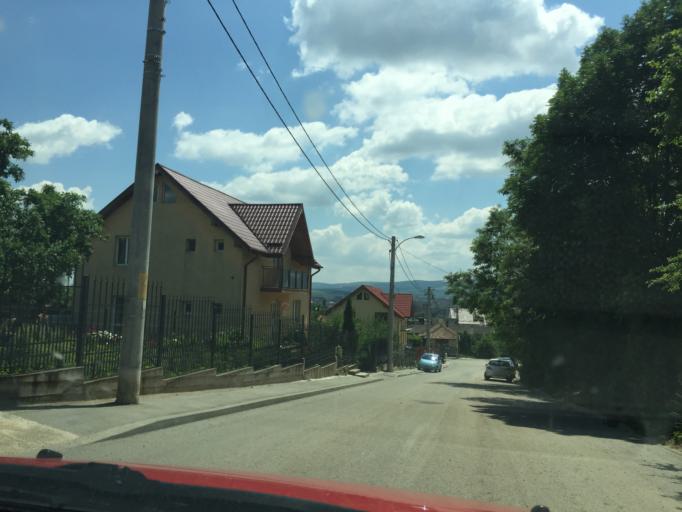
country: RO
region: Cluj
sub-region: Municipiul Cluj-Napoca
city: Cluj-Napoca
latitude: 46.7979
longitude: 23.6022
